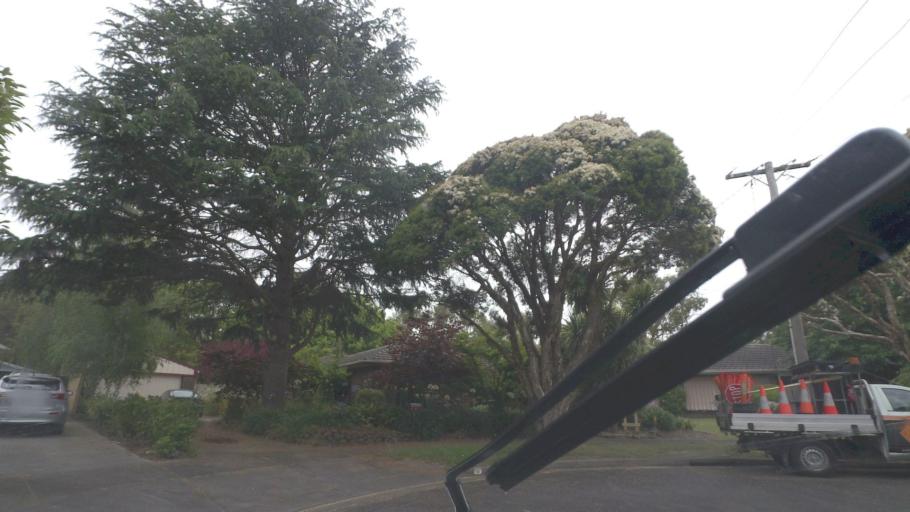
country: AU
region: Victoria
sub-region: Maroondah
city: Croydon North
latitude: -37.7793
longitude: 145.3055
